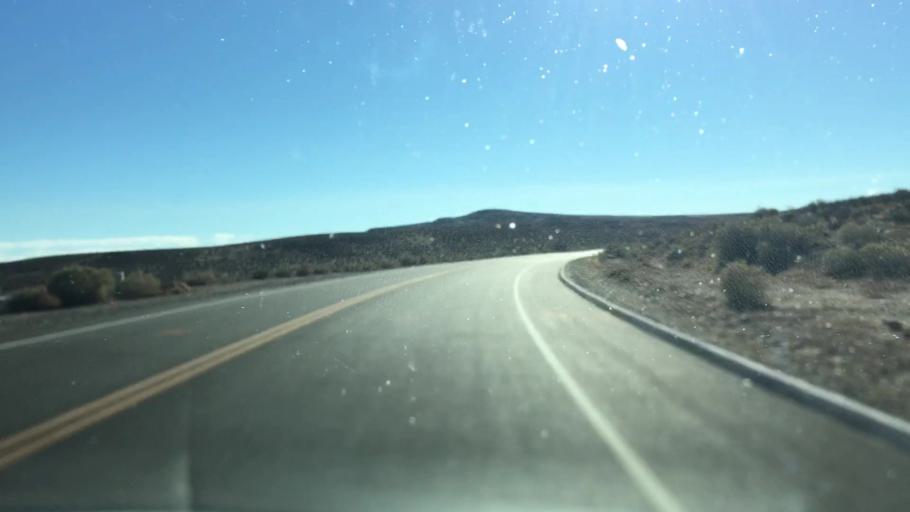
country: US
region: Arizona
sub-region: Coconino County
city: Page
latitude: 36.9907
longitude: -111.4913
